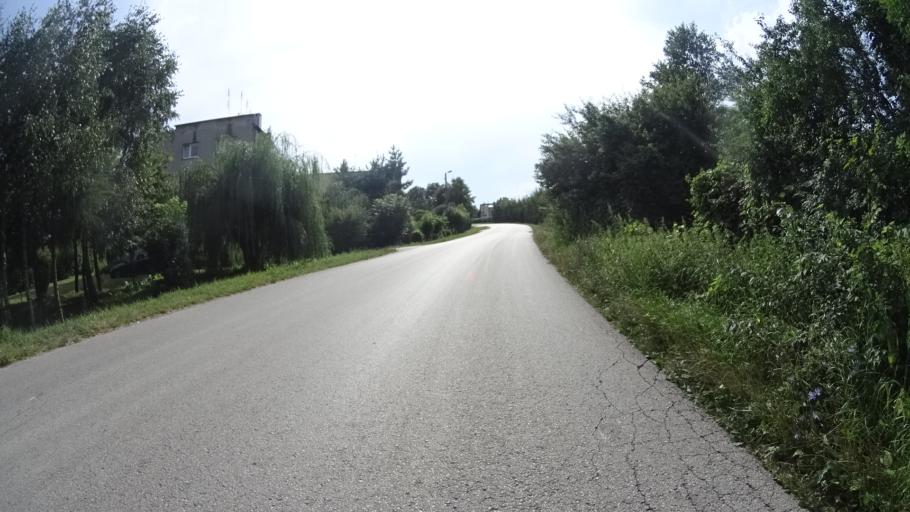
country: PL
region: Masovian Voivodeship
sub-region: Powiat grojecki
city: Goszczyn
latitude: 51.6937
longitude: 20.8195
